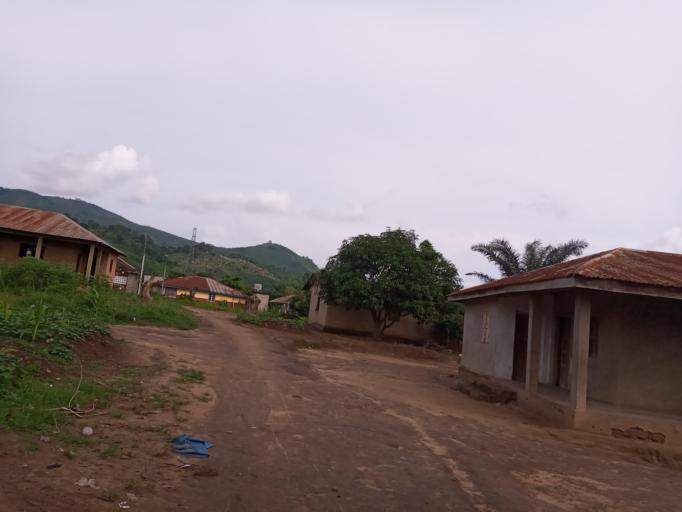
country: SL
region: Northern Province
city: Bumbuna
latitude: 9.0483
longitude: -11.7567
